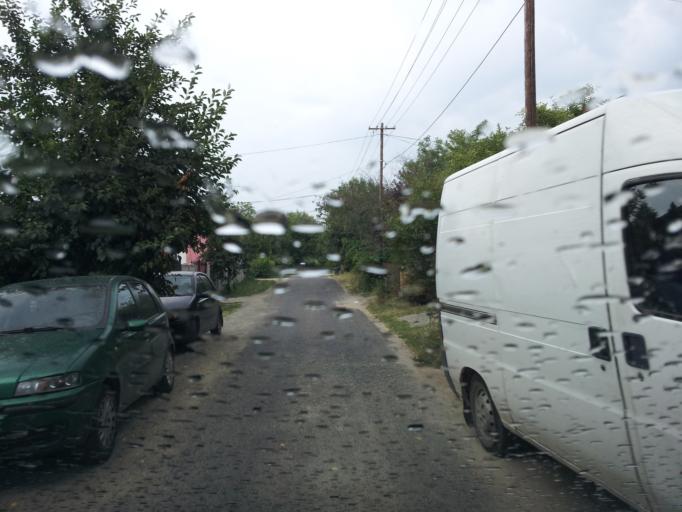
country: HU
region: Pest
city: Szigethalom
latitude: 47.3092
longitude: 19.0355
